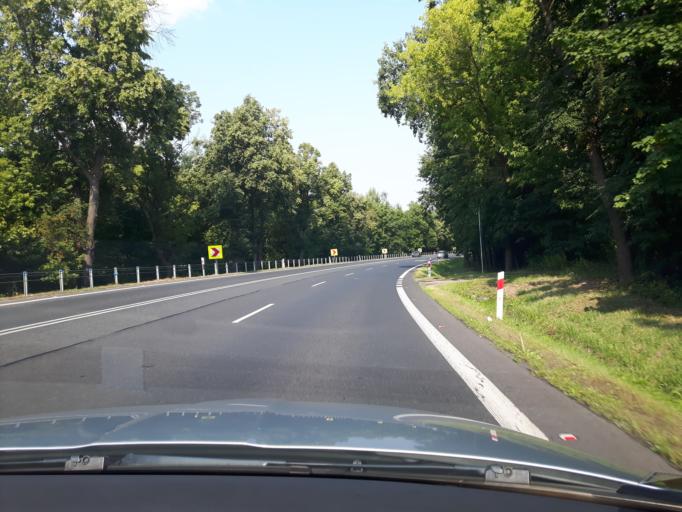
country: PL
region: Masovian Voivodeship
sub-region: Powiat nowodworski
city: Nowy Dwor Mazowiecki
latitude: 52.4465
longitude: 20.6677
